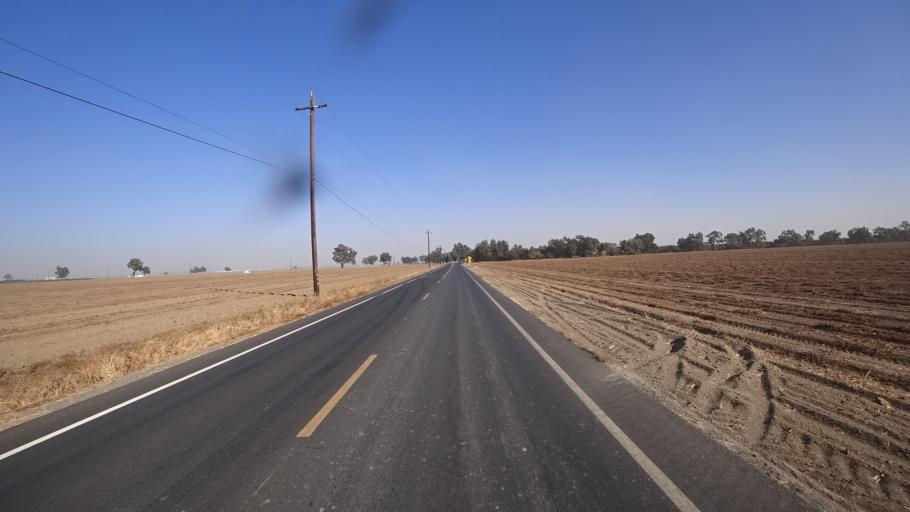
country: US
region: California
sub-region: Yolo County
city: Woodland
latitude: 38.7350
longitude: -121.7693
